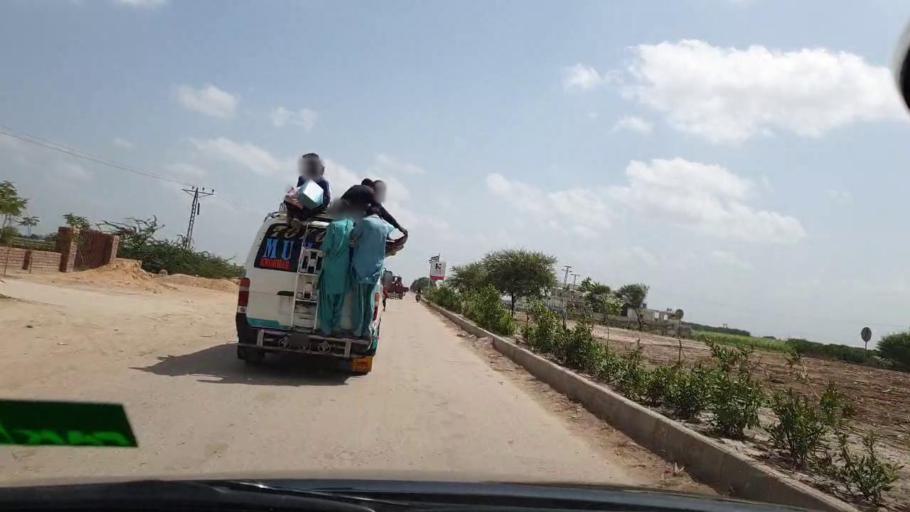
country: PK
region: Sindh
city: Kadhan
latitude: 24.6275
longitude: 69.1900
